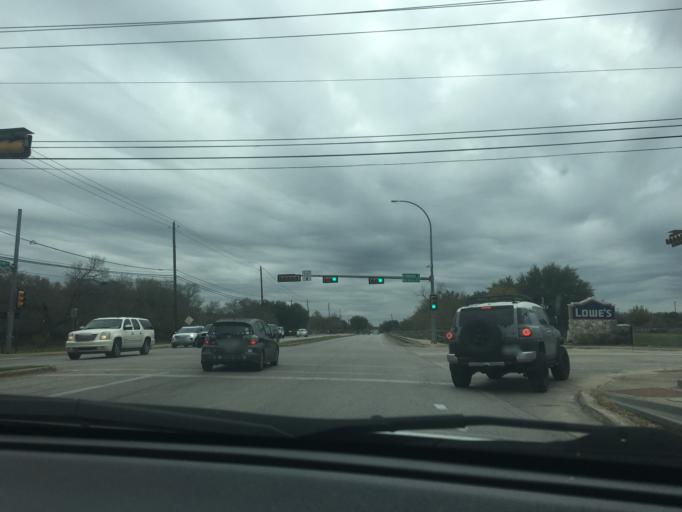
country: US
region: Texas
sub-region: Travis County
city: Shady Hollow
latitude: 30.2201
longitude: -97.8266
